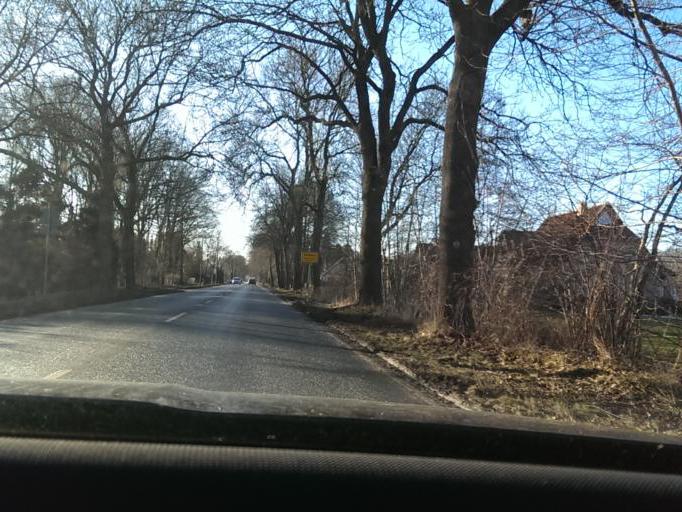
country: DE
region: Lower Saxony
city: Elze
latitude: 52.5699
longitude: 9.7264
